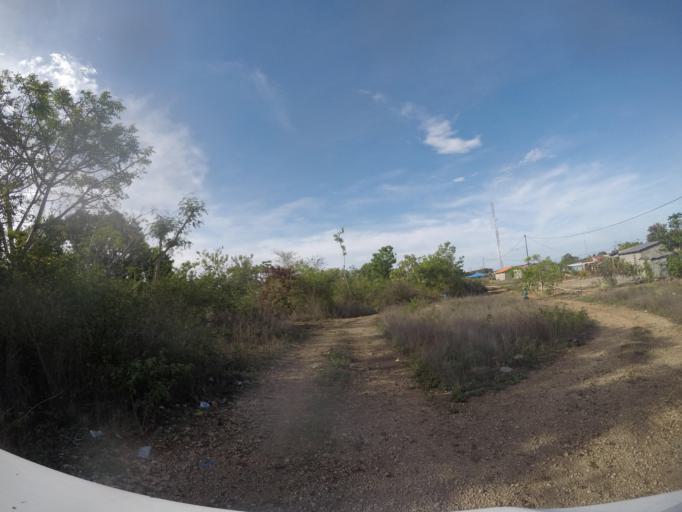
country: TL
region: Baucau
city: Baucau
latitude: -8.4891
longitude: 126.4532
